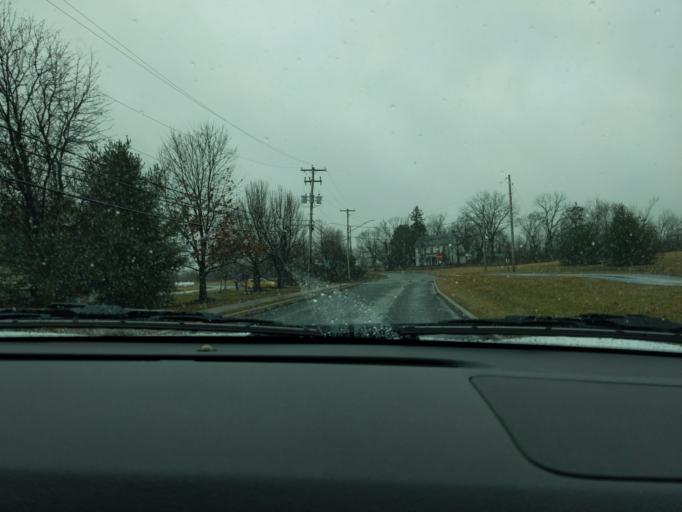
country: US
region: Pennsylvania
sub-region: Bucks County
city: Spinnerstown
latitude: 40.4327
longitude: -75.4111
